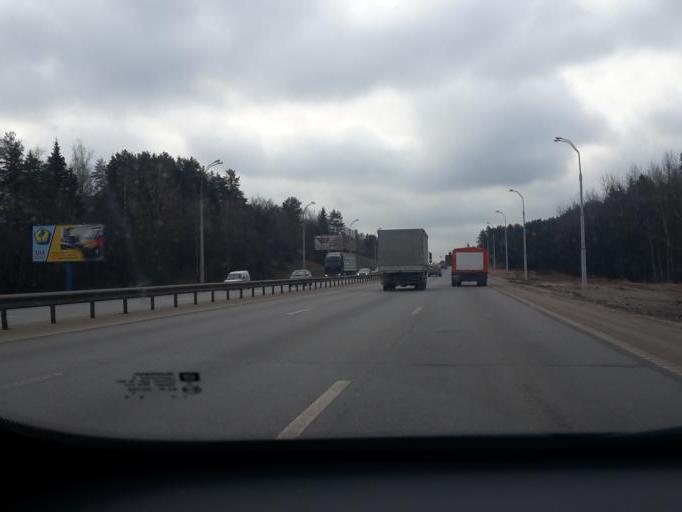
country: BY
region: Minsk
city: Borovlyany
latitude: 53.9304
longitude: 27.6773
